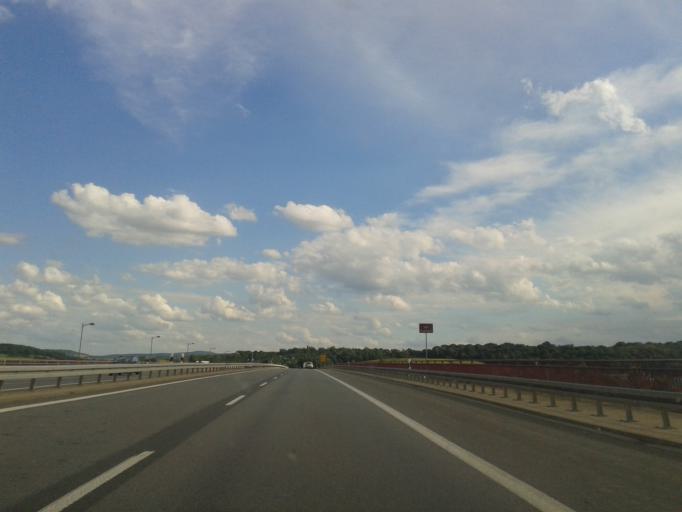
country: DE
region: Saxony
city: Pirna
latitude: 50.9648
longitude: 13.9155
